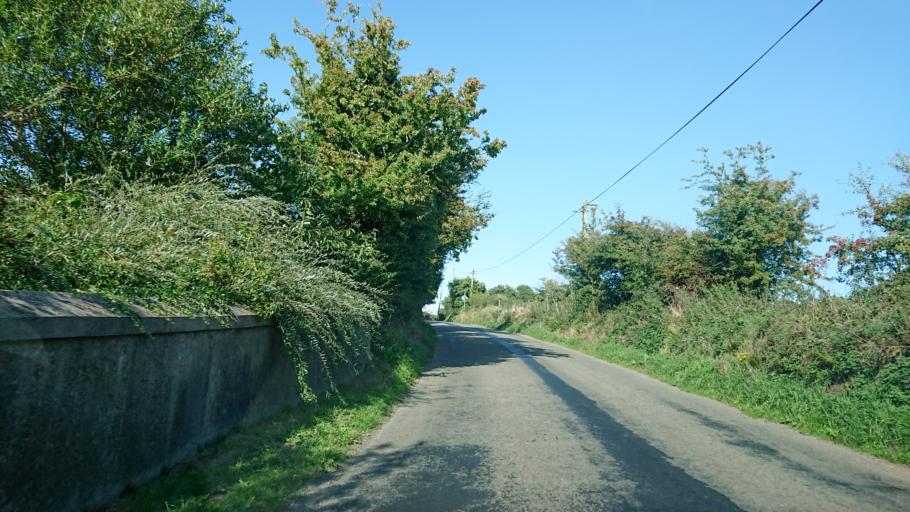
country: IE
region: Munster
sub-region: Waterford
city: Dunmore East
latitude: 52.1835
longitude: -7.0036
